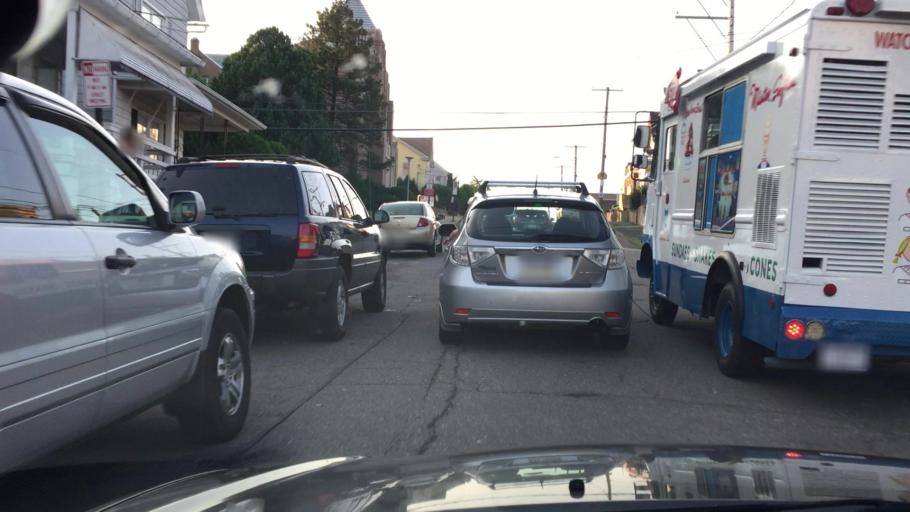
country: US
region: Pennsylvania
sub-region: Luzerne County
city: Hazleton
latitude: 40.9644
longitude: -75.9704
